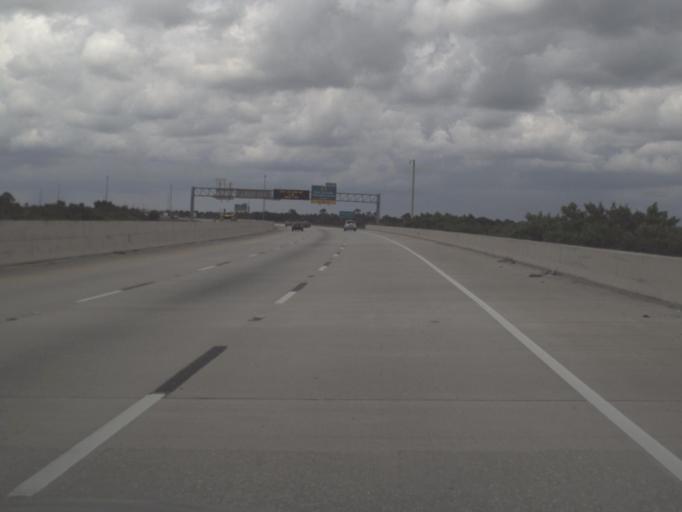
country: US
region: Florida
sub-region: Charlotte County
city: Harbour Heights
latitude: 26.9702
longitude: -82.0195
